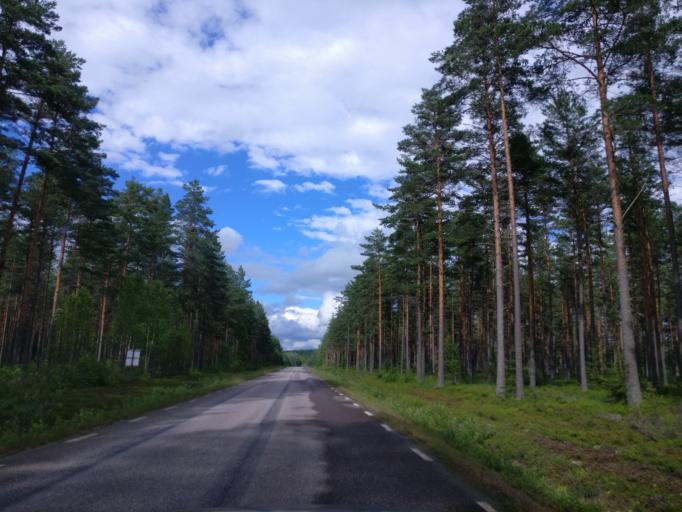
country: SE
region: Vaermland
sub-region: Hagfors Kommun
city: Ekshaerad
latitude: 60.0405
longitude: 13.5145
